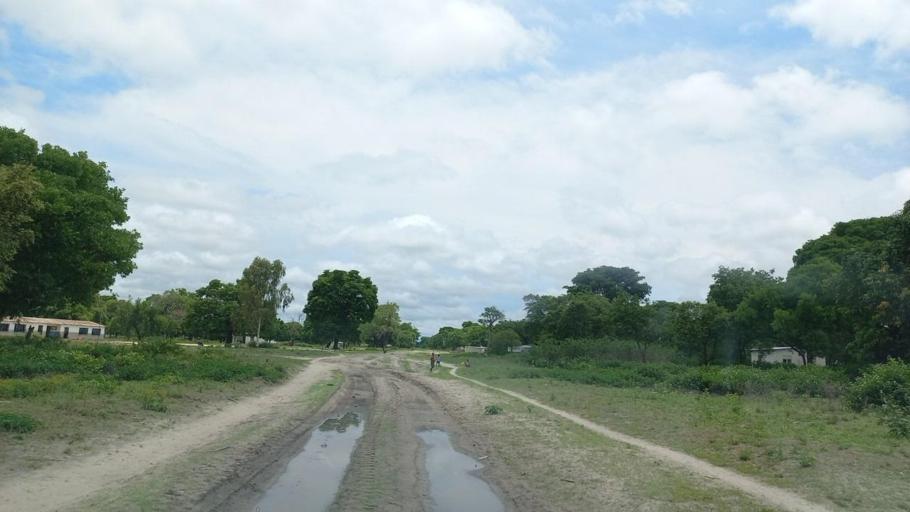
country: ZM
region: North-Western
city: Kabompo
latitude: -13.1888
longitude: 23.9584
